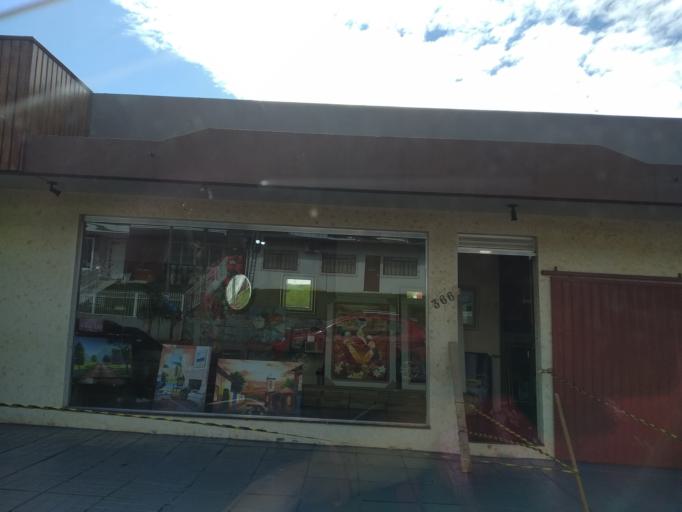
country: BR
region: Parana
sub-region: Pato Branco
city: Pato Branco
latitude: -26.2305
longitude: -52.6680
